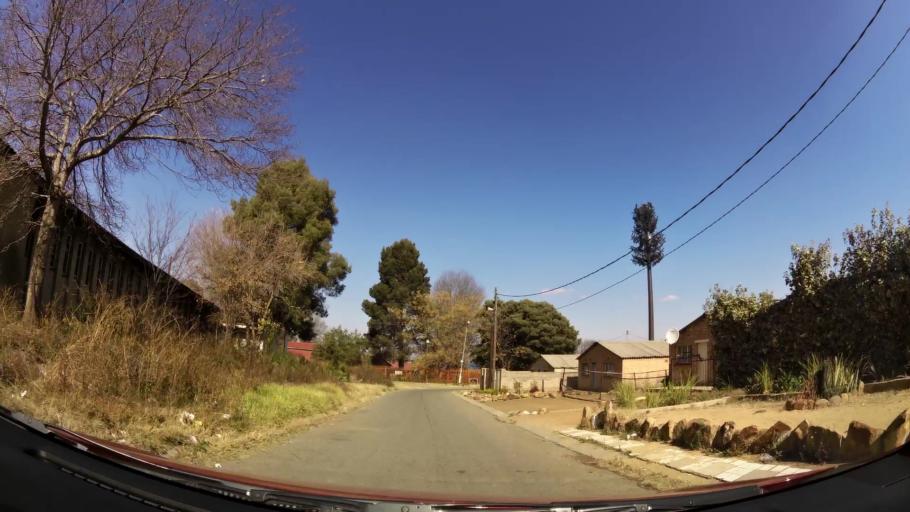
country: ZA
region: Gauteng
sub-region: City of Johannesburg Metropolitan Municipality
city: Soweto
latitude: -26.2414
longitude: 27.8969
